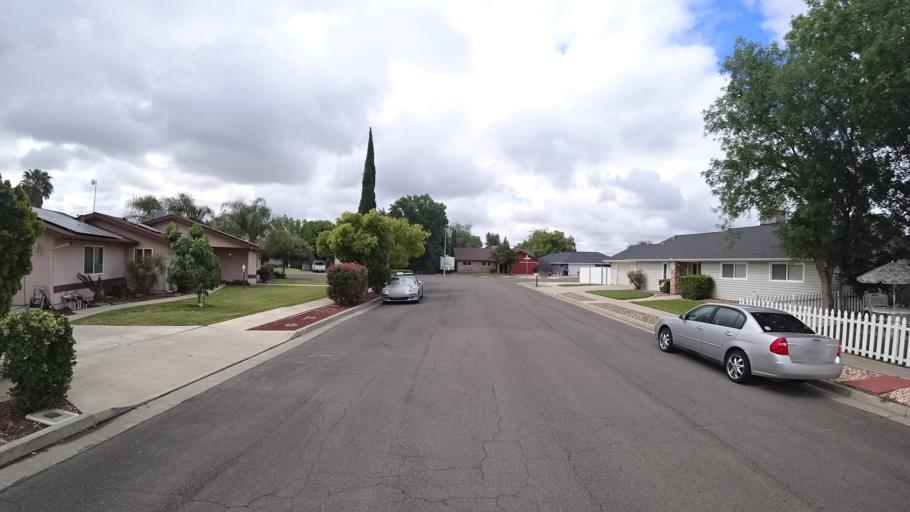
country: US
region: California
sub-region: Kings County
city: Hanford
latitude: 36.3459
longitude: -119.6613
